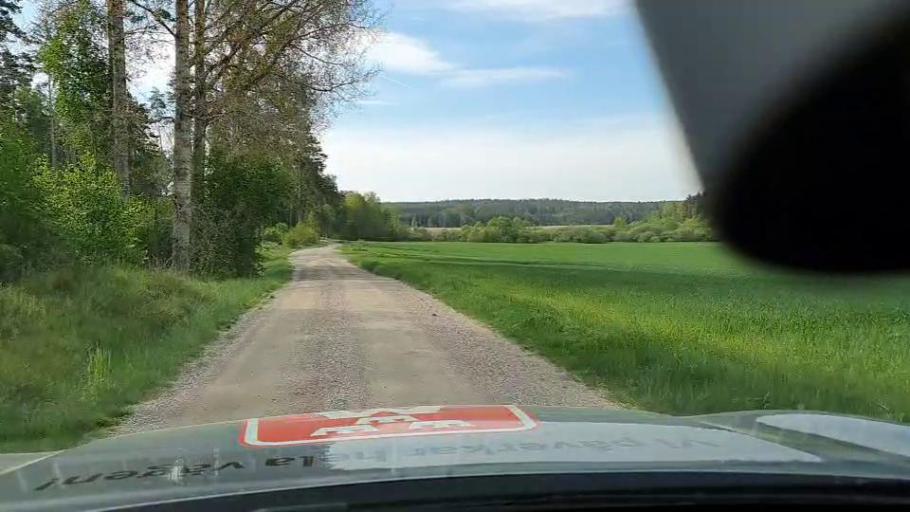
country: SE
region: Soedermanland
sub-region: Strangnas Kommun
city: Akers Styckebruk
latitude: 59.2435
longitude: 16.9339
